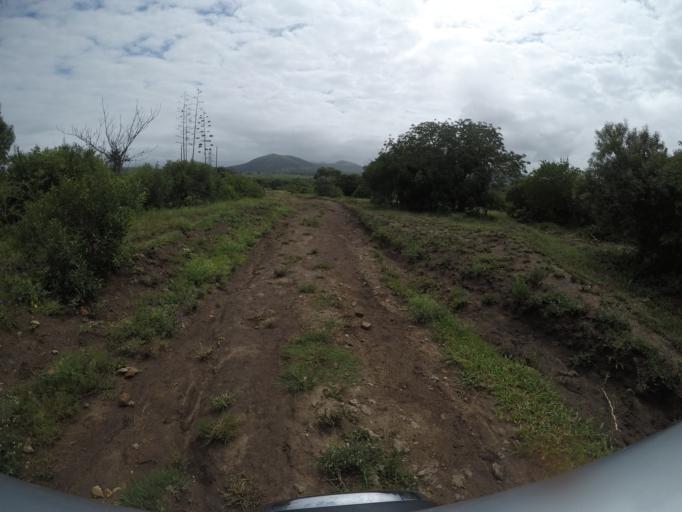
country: ZA
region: KwaZulu-Natal
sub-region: uThungulu District Municipality
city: Empangeni
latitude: -28.6244
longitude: 31.8647
